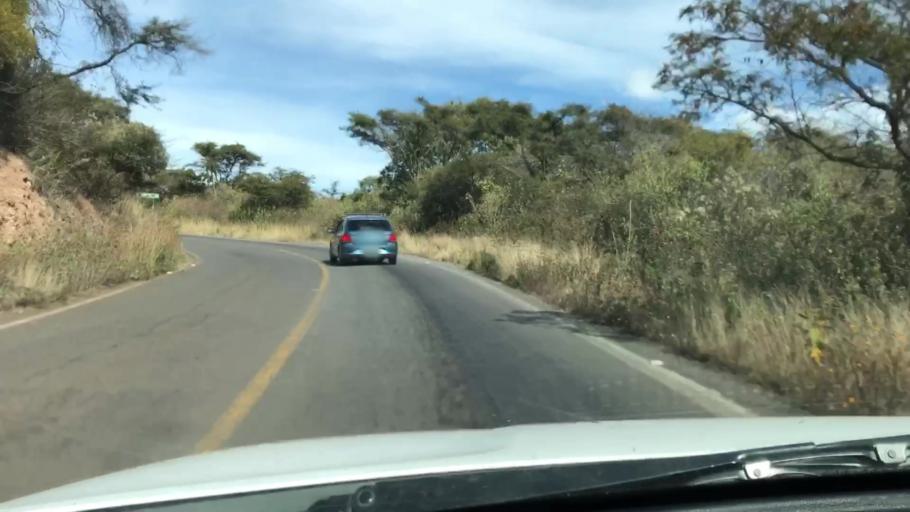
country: MX
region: Jalisco
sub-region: Zacoalco de Torres
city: Barranca de Otates (Barranca de Otatan)
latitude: 20.1941
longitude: -103.6935
